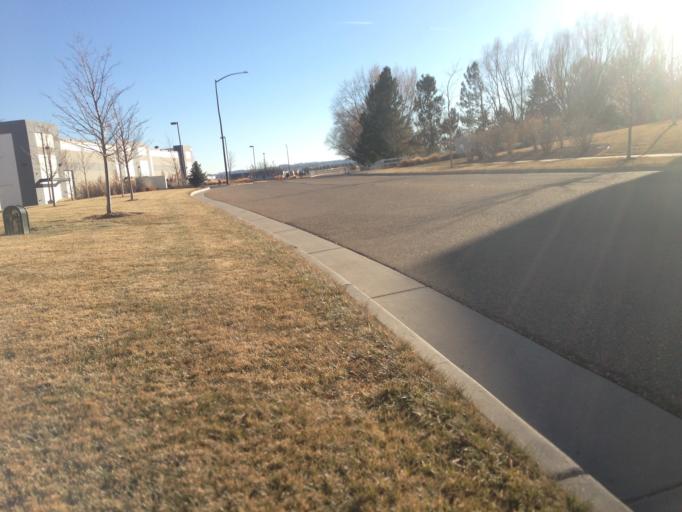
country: US
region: Colorado
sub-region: Boulder County
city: Louisville
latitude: 39.9647
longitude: -105.1123
